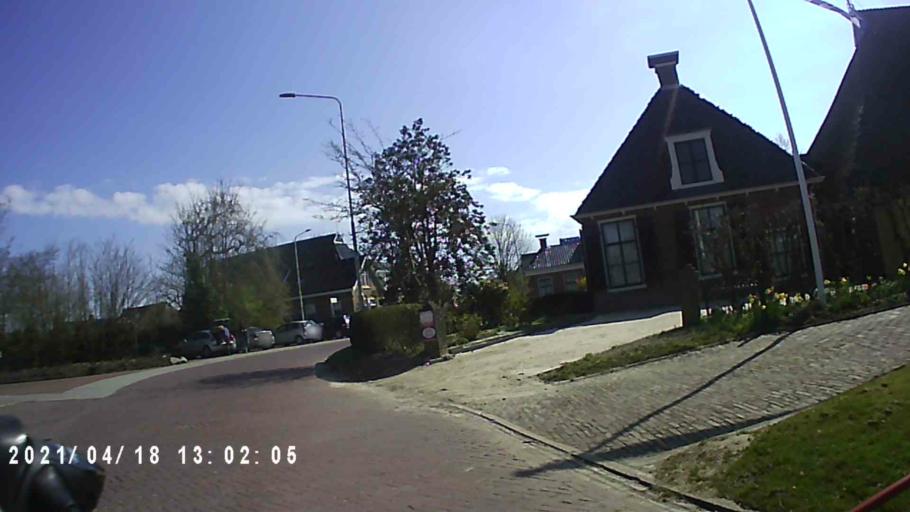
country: NL
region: Friesland
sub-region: Gemeente Dongeradeel
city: Anjum
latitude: 53.4015
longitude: 6.0862
